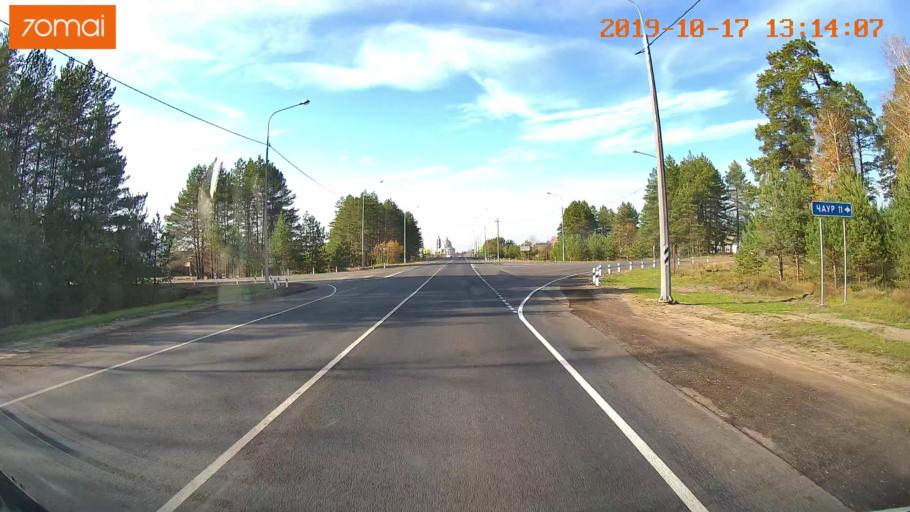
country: RU
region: Rjazan
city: Gus'-Zheleznyy
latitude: 55.0504
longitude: 41.1769
